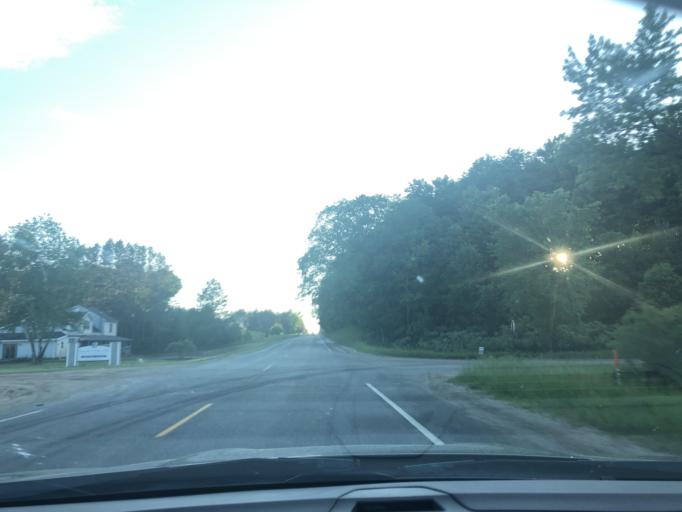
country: US
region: Michigan
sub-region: Missaukee County
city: Lake City
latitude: 44.4673
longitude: -85.1346
